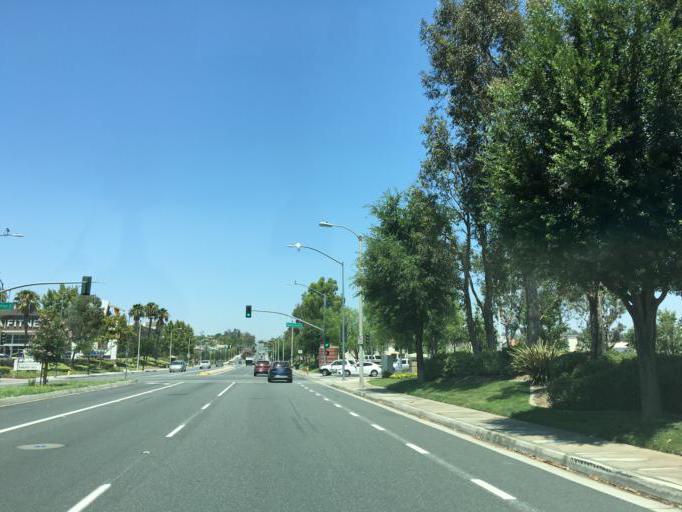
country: US
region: California
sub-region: Los Angeles County
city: Santa Clarita
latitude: 34.3823
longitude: -118.5710
